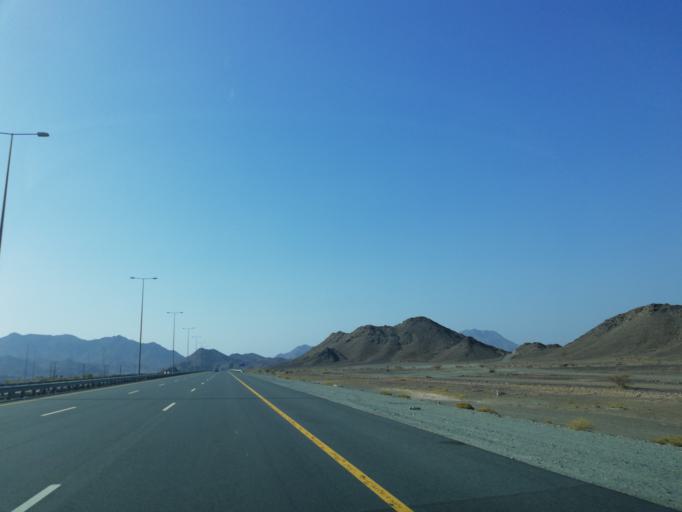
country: OM
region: Ash Sharqiyah
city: Ibra'
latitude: 22.9313
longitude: 58.2558
